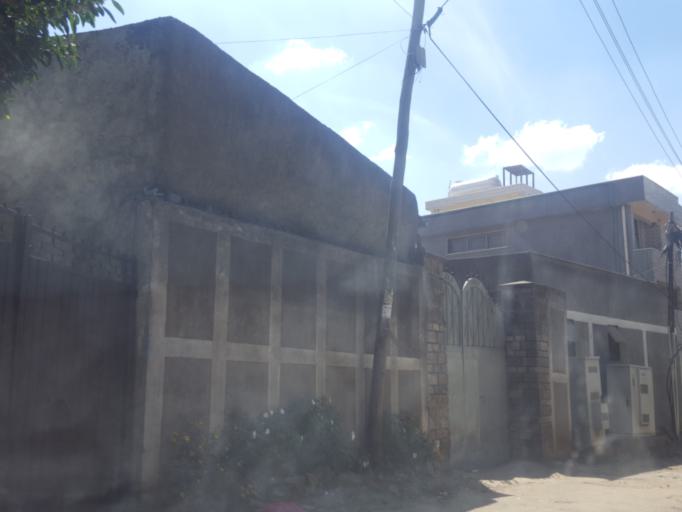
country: ET
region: Adis Abeba
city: Addis Ababa
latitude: 9.0502
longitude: 38.7320
